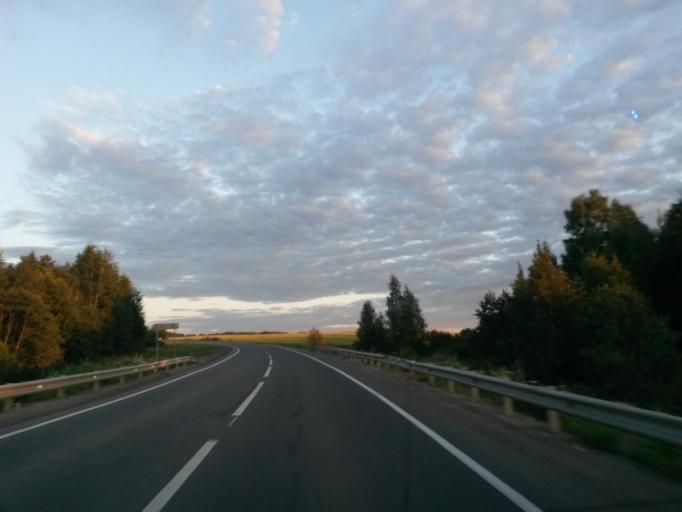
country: RU
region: Jaroslavl
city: Gavrilov-Yam
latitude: 57.3282
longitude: 39.9214
